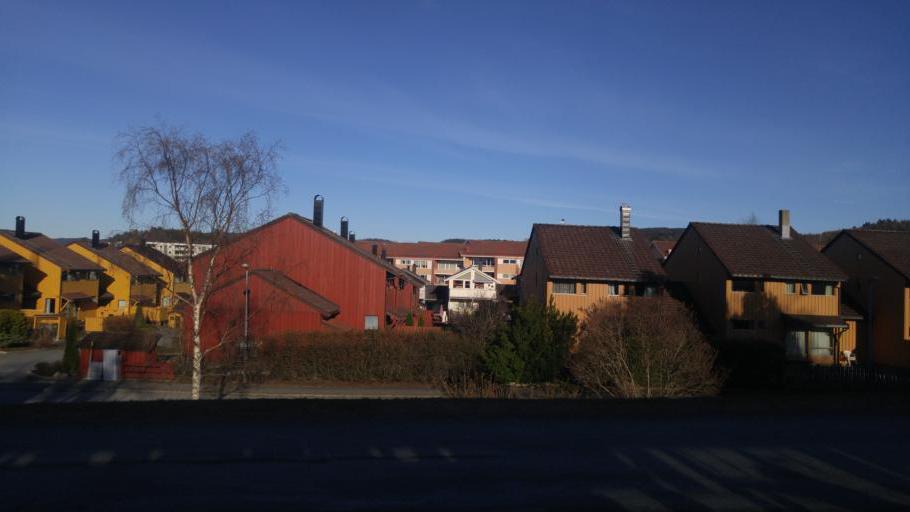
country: NO
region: Sor-Trondelag
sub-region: Trondheim
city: Trondheim
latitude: 63.4164
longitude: 10.4465
